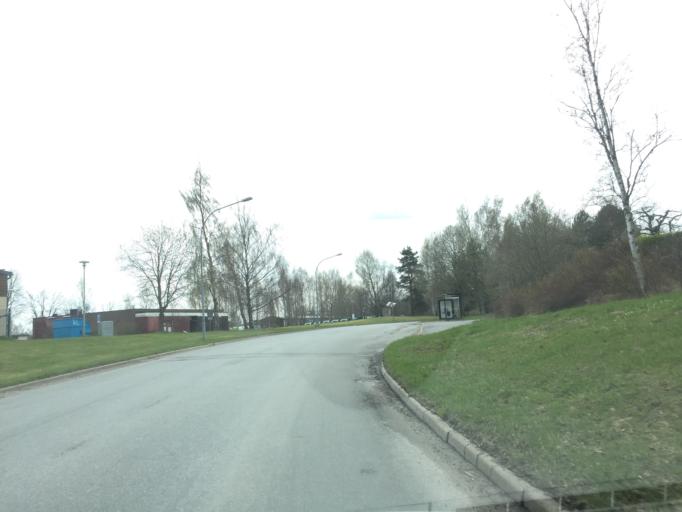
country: SE
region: OErebro
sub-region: Orebro Kommun
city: Orebro
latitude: 59.3099
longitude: 15.1847
